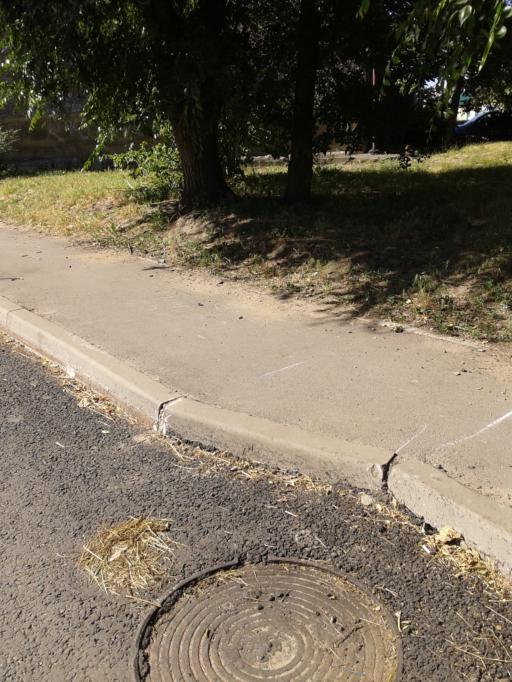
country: RU
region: Voronezj
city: Pridonskoy
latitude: 51.6602
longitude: 39.1206
